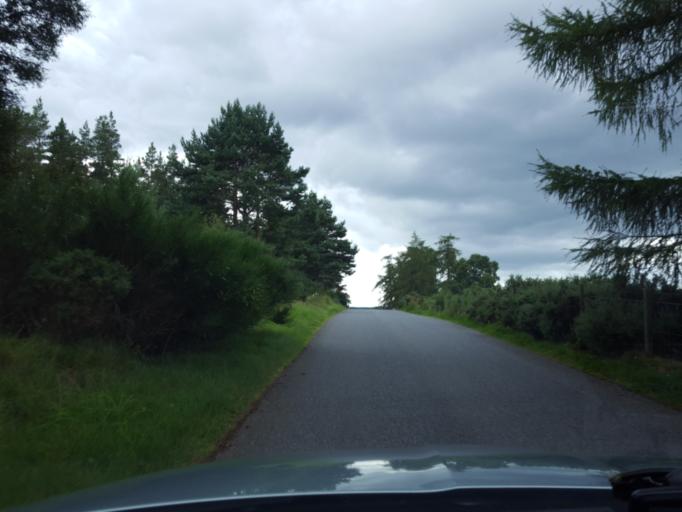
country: GB
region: Scotland
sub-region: Highland
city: Grantown on Spey
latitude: 57.3898
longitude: -3.4599
